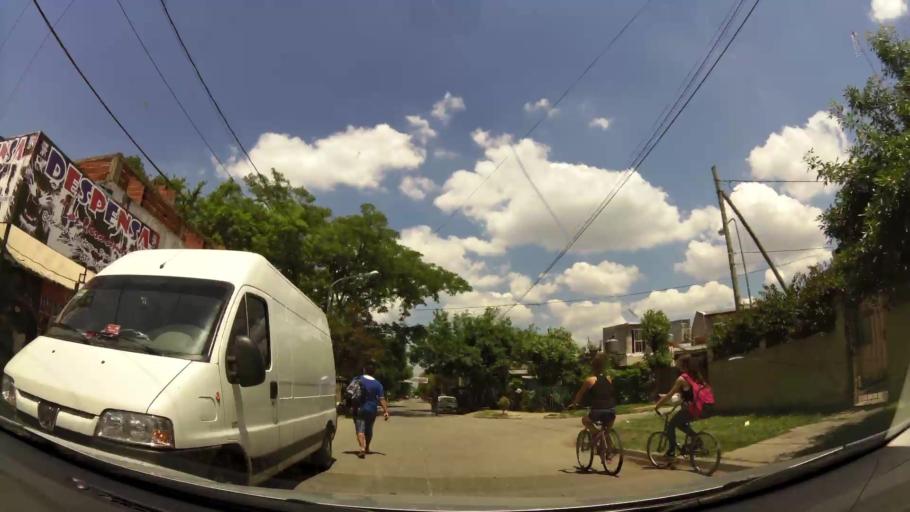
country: AR
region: Buenos Aires
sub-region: Partido de Tigre
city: Tigre
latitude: -34.4104
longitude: -58.6042
